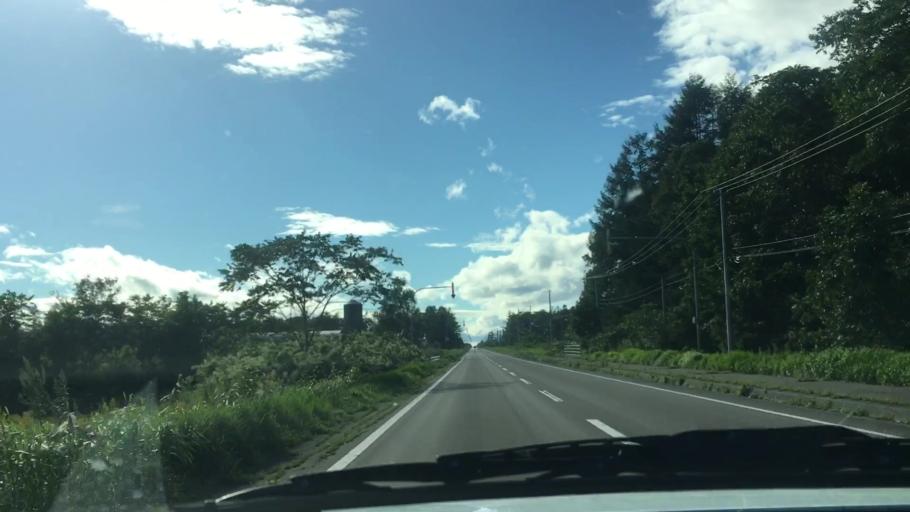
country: JP
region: Hokkaido
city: Otofuke
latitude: 43.1571
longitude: 143.1818
